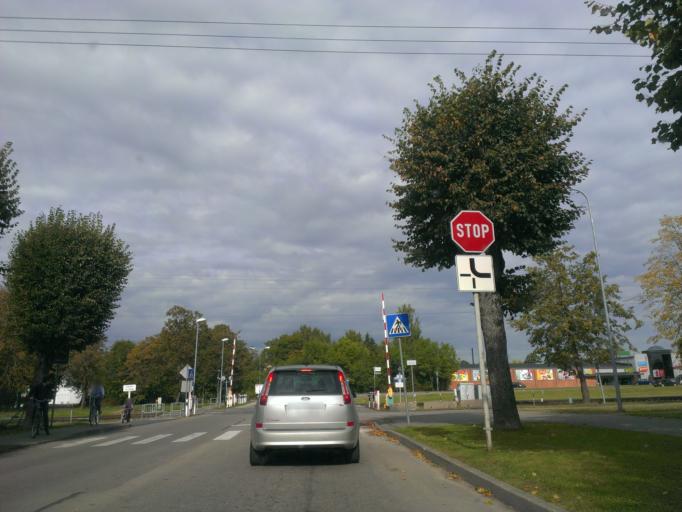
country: LV
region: Sigulda
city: Sigulda
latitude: 57.1515
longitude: 24.8471
